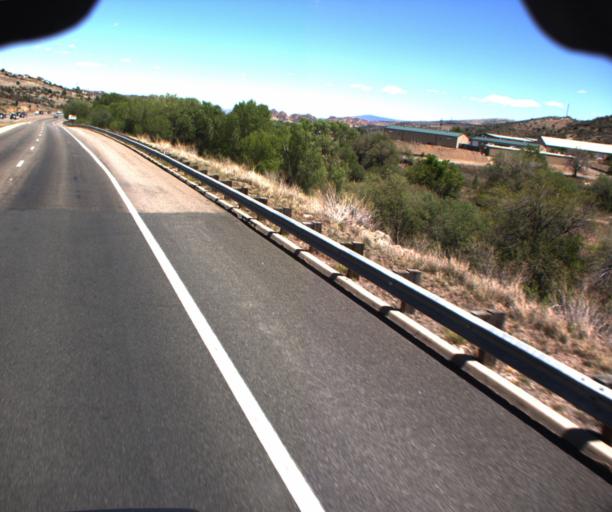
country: US
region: Arizona
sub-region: Yavapai County
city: Prescott
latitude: 34.5616
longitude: -112.4454
